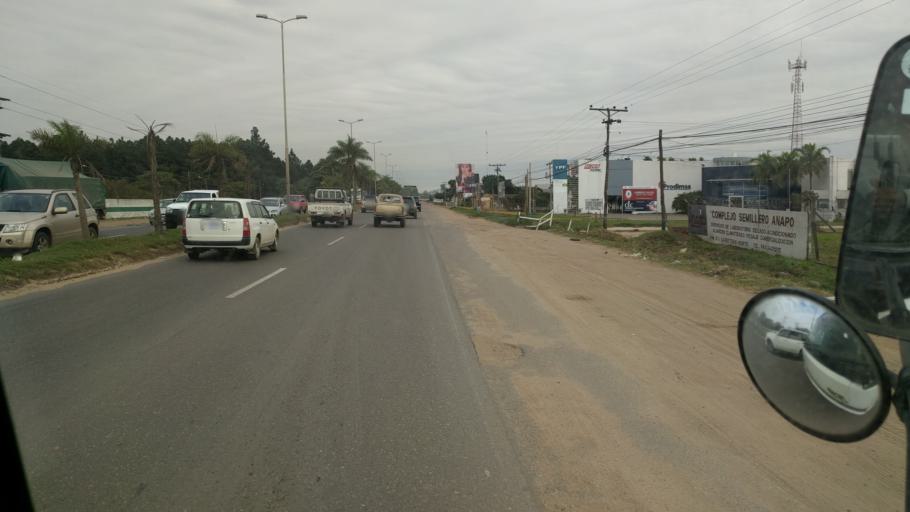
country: BO
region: Santa Cruz
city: Santa Cruz de la Sierra
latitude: -17.7010
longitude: -63.1598
